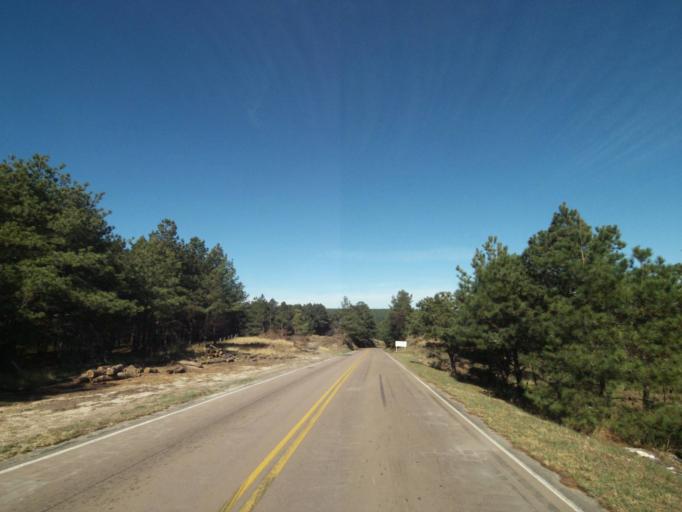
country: BR
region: Parana
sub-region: Tibagi
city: Tibagi
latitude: -24.6077
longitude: -50.2585
